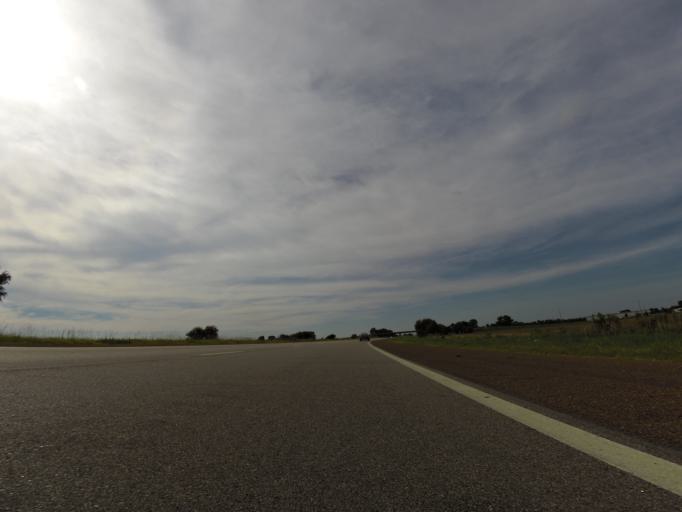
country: US
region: Kansas
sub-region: Sedgwick County
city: Maize
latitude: 37.7622
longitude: -97.4463
